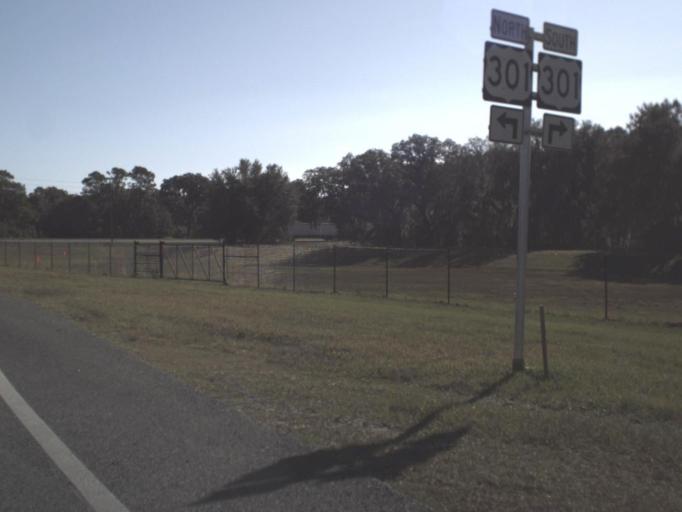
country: US
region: Florida
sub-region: Marion County
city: Belleview
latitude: 29.0292
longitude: -82.0471
